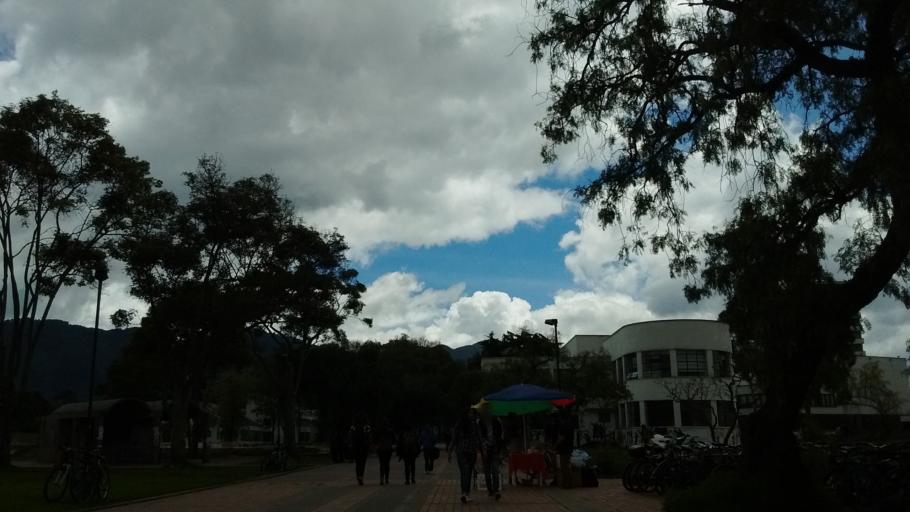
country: CO
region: Bogota D.C.
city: Bogota
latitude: 4.6372
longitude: -74.0826
